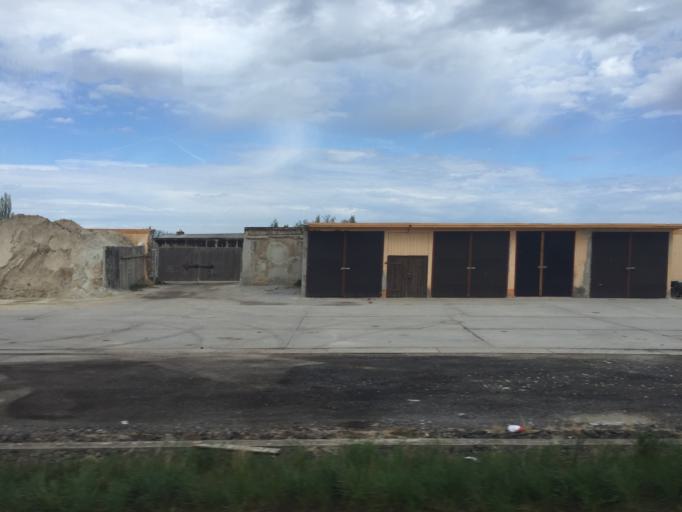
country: DE
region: Saxony
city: Kubschutz
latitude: 51.1646
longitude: 14.5064
